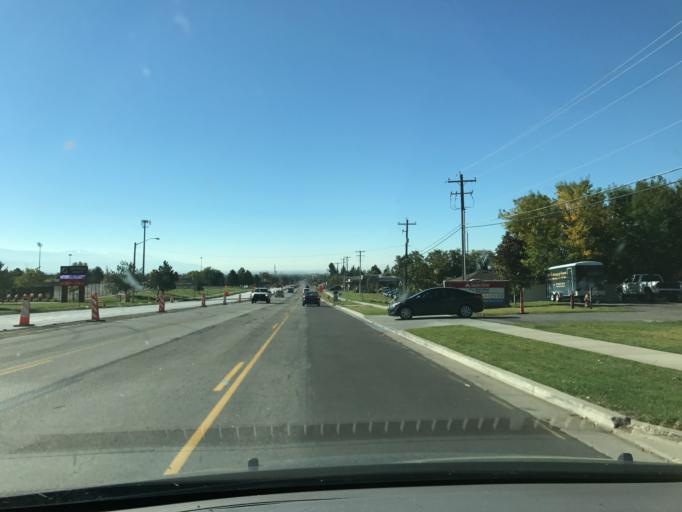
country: US
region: Utah
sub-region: Davis County
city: Hill Air Force Bace
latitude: 41.0950
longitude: -111.9736
